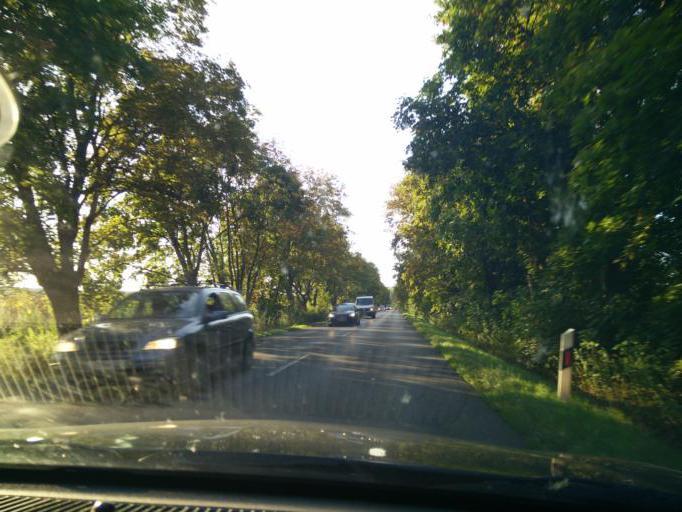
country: HU
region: Pest
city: Zsambek
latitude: 47.5318
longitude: 18.7317
